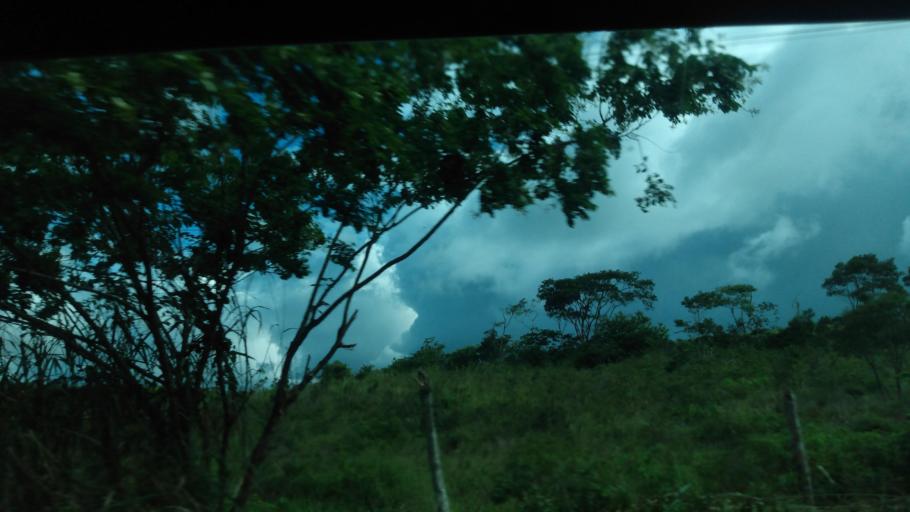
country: BR
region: Pernambuco
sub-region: Quipapa
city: Quipapa
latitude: -8.7783
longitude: -35.9407
